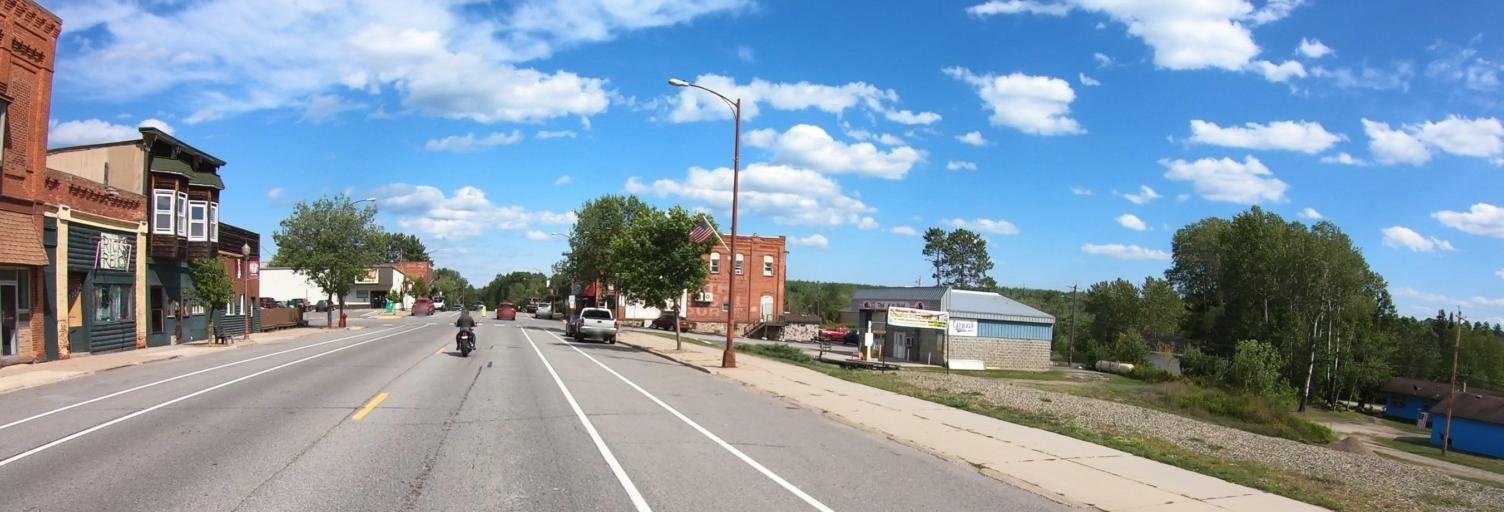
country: US
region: Minnesota
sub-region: Saint Louis County
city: Aurora
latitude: 47.8052
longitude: -92.2738
